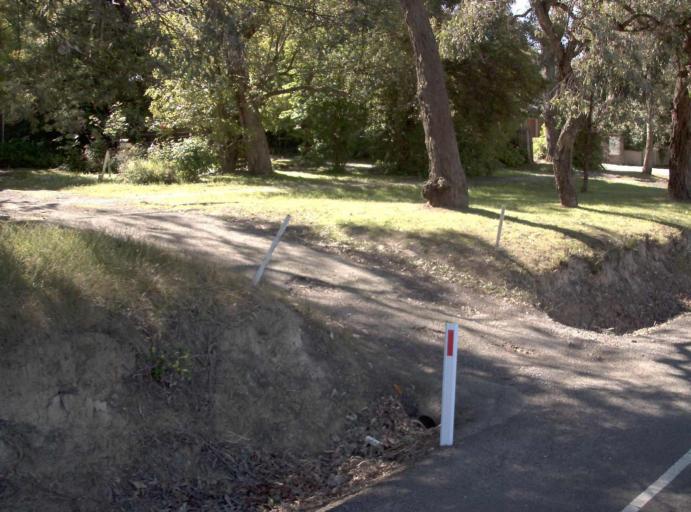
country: AU
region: Victoria
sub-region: Maroondah
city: Croydon South
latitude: -37.8035
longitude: 145.2730
